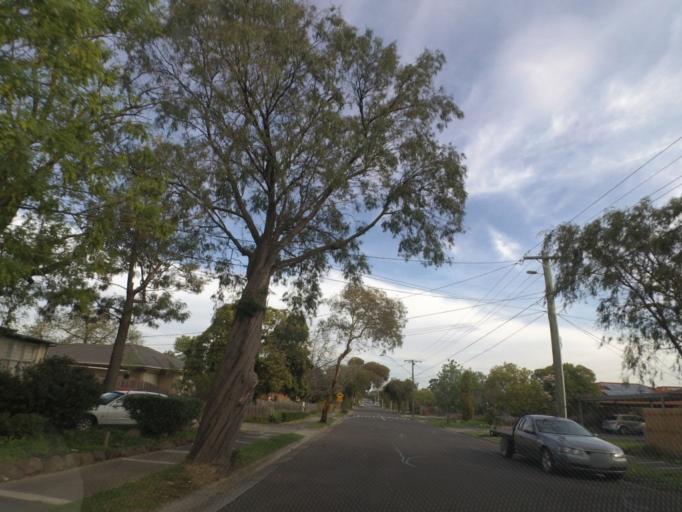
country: AU
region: Victoria
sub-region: Knox
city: Knoxfield
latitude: -37.8917
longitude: 145.2405
